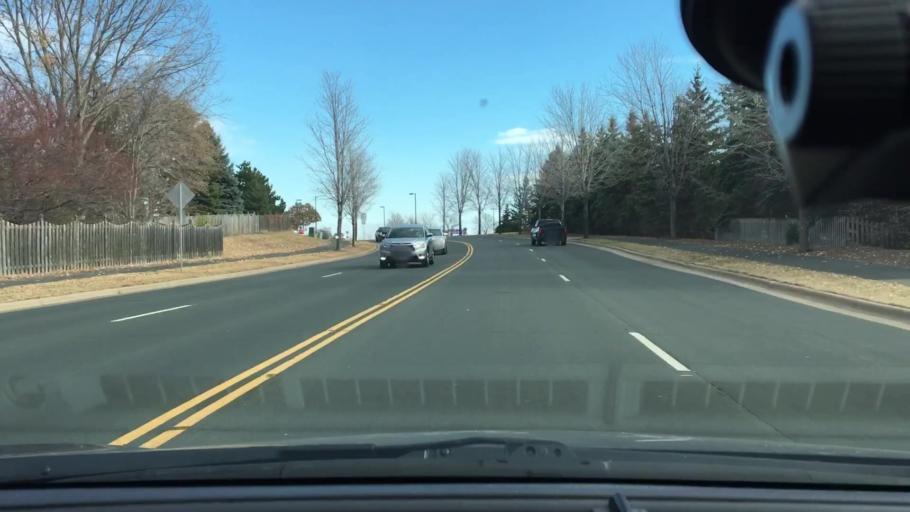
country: US
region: Minnesota
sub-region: Hennepin County
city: Maple Grove
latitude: 45.1026
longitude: -93.4734
